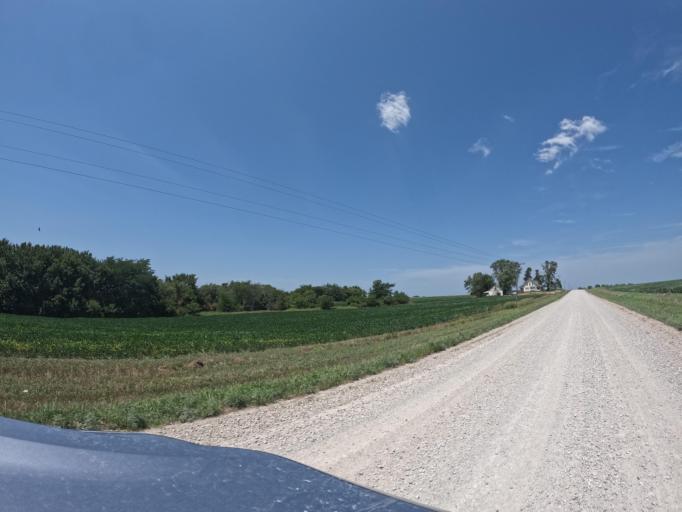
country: US
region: Iowa
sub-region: Henry County
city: Mount Pleasant
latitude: 40.9353
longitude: -91.6457
